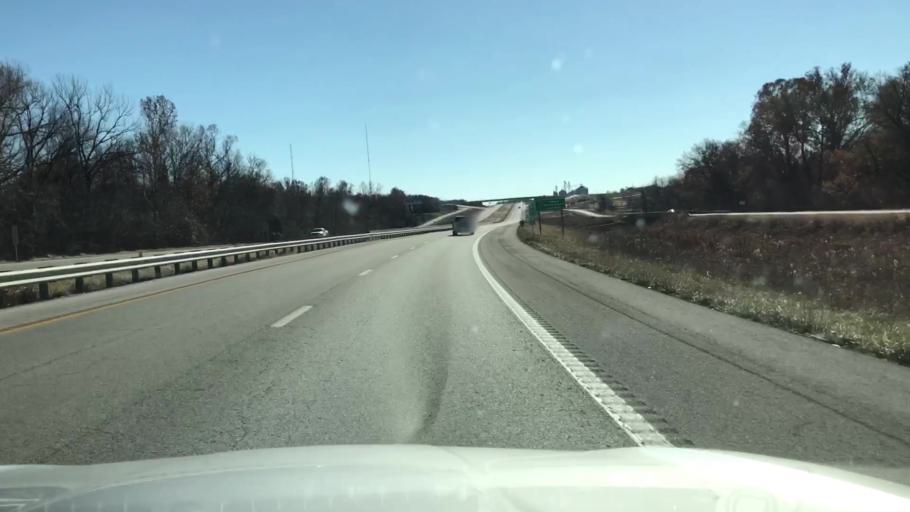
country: US
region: Missouri
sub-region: Jasper County
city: Carthage
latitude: 37.1078
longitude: -94.3101
